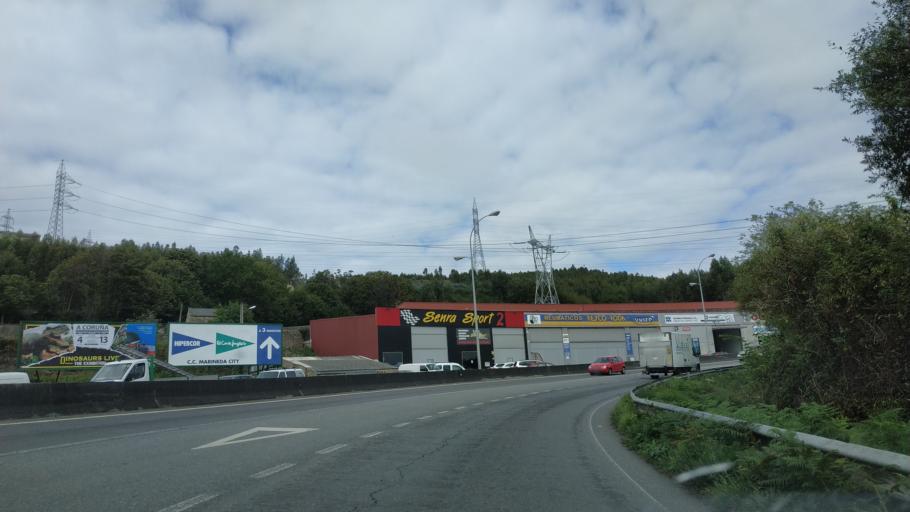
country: ES
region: Galicia
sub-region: Provincia da Coruna
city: Arteixo
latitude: 43.3242
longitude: -8.4757
